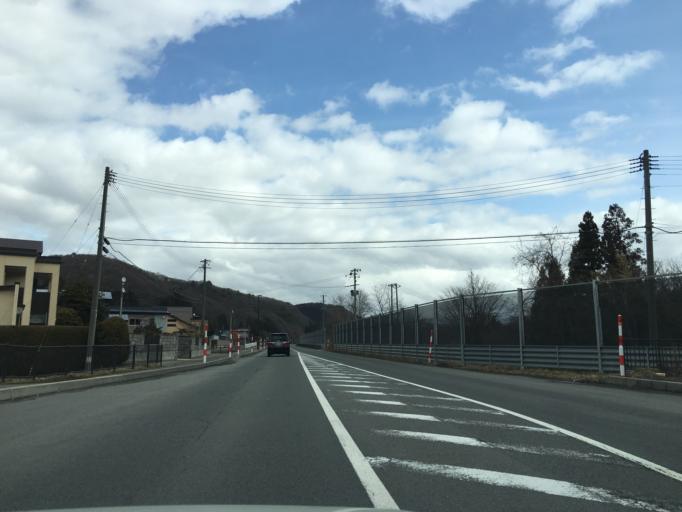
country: JP
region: Akita
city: Hanawa
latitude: 40.2334
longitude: 140.6955
